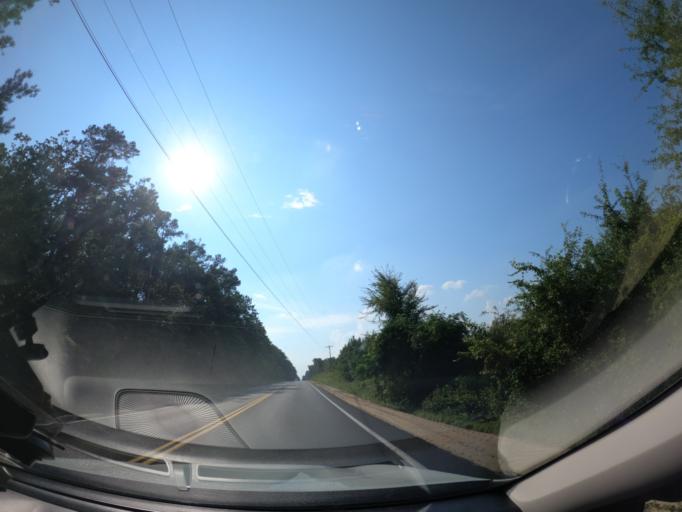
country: US
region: South Carolina
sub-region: Aiken County
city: New Ellenton
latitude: 33.3993
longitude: -81.7568
